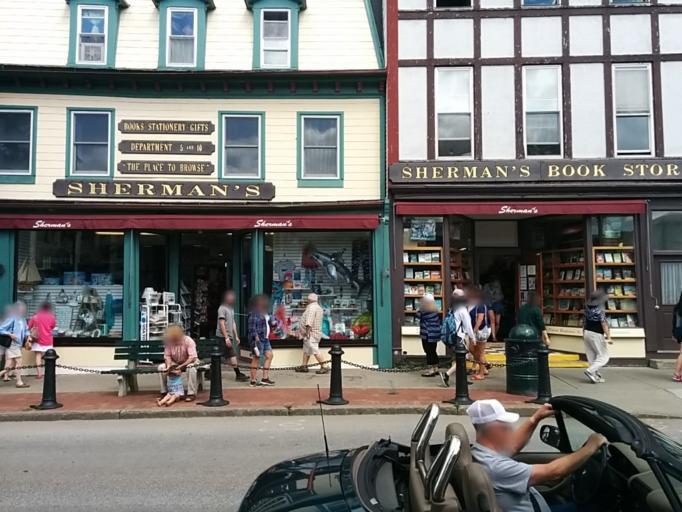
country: US
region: Maine
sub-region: Hancock County
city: Bar Harbor
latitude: 44.3900
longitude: -68.2049
